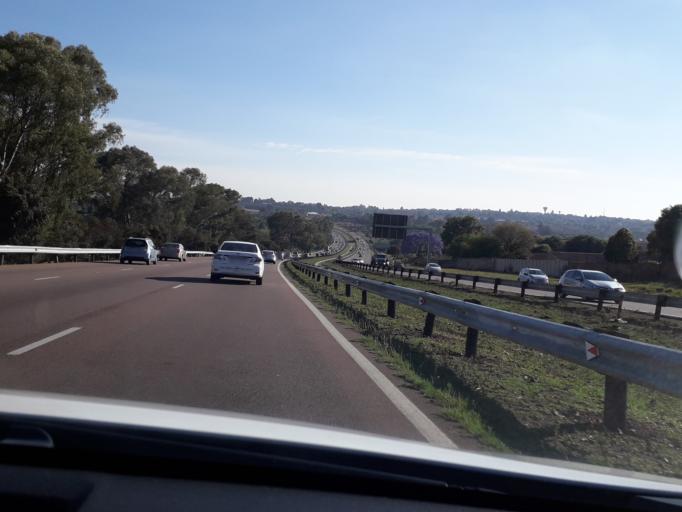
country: ZA
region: Gauteng
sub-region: City of Tshwane Metropolitan Municipality
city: Centurion
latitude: -25.8534
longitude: 28.1754
